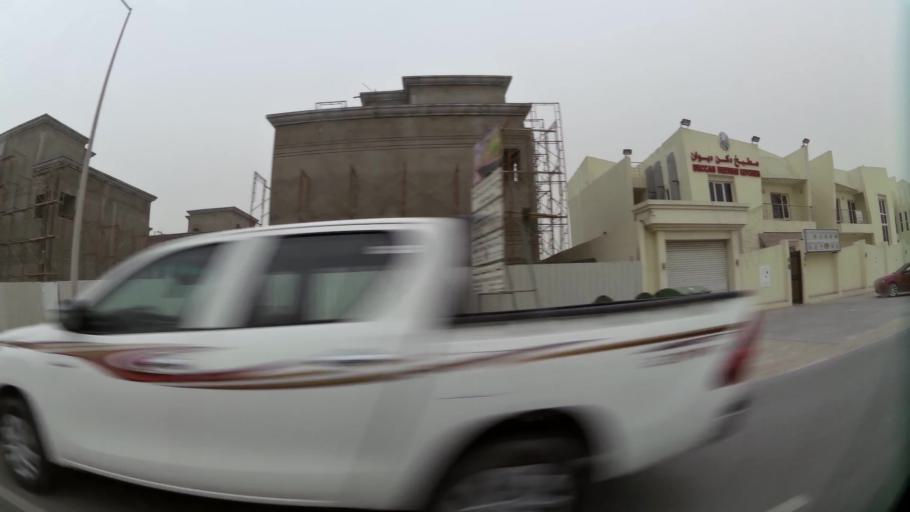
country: QA
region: Baladiyat ad Dawhah
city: Doha
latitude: 25.2403
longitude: 51.4838
